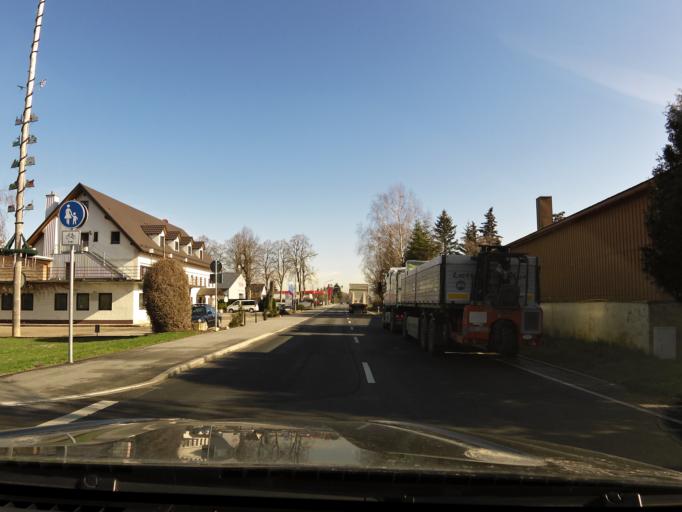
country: DE
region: Bavaria
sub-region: Upper Bavaria
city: Hallbergmoos
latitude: 48.3426
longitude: 11.7089
